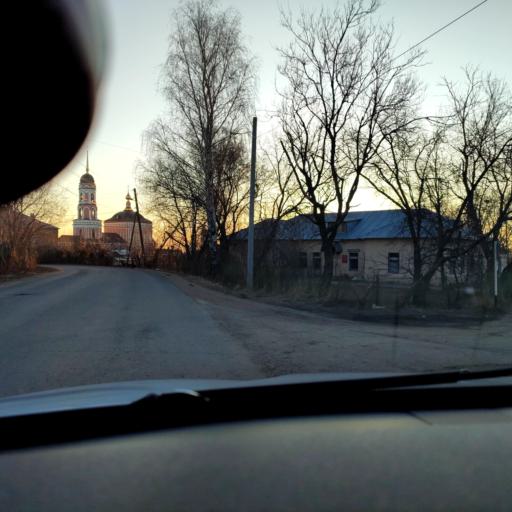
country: RU
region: Perm
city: Kultayevo
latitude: 57.9344
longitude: 55.8810
